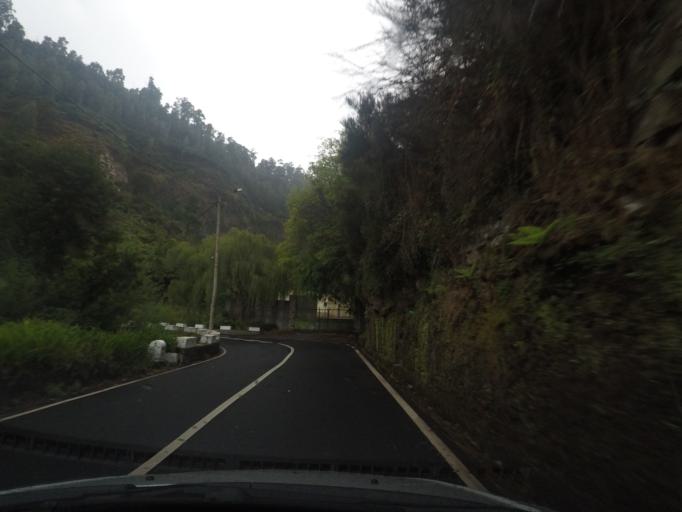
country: PT
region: Madeira
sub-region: Santa Cruz
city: Camacha
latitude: 32.7048
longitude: -16.8426
